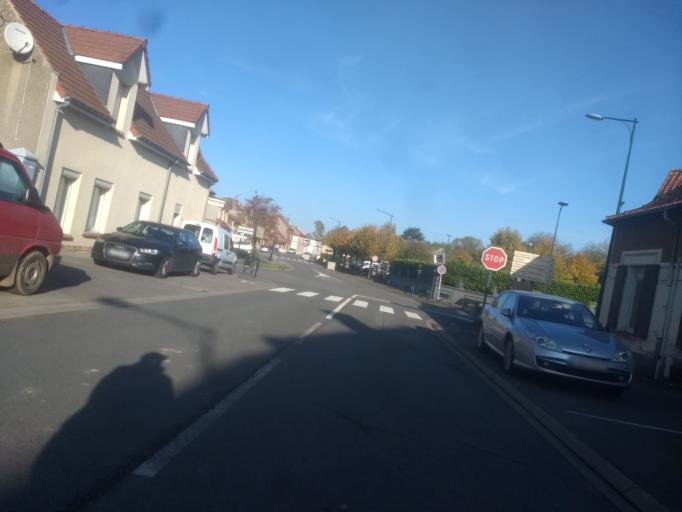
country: FR
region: Nord-Pas-de-Calais
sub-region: Departement du Pas-de-Calais
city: Tilloy-les-Mofflaines
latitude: 50.2743
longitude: 2.8160
